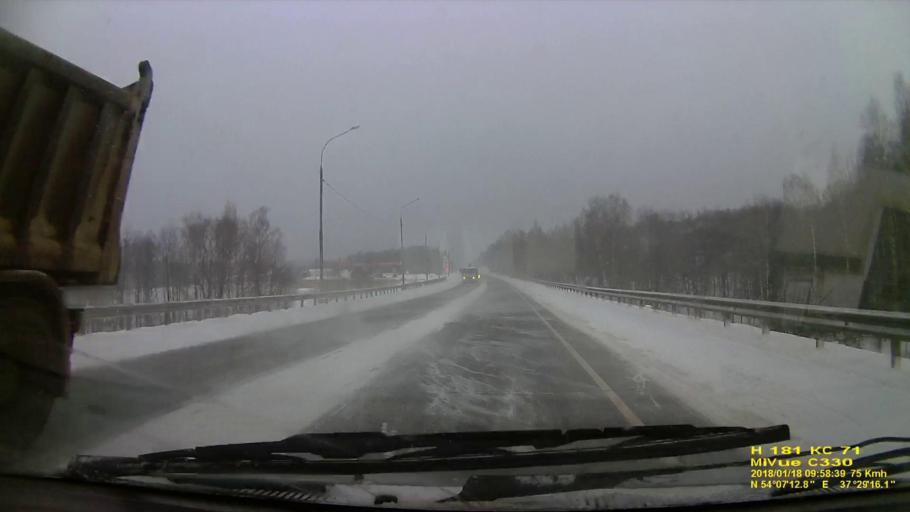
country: RU
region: Tula
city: Kosaya Gora
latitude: 54.1202
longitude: 37.4878
